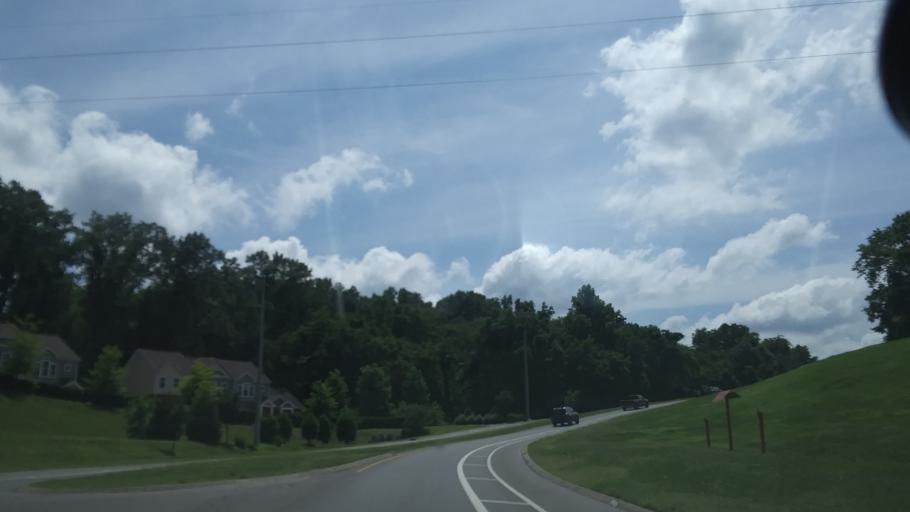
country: US
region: Tennessee
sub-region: Rutherford County
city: La Vergne
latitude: 36.0887
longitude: -86.6440
